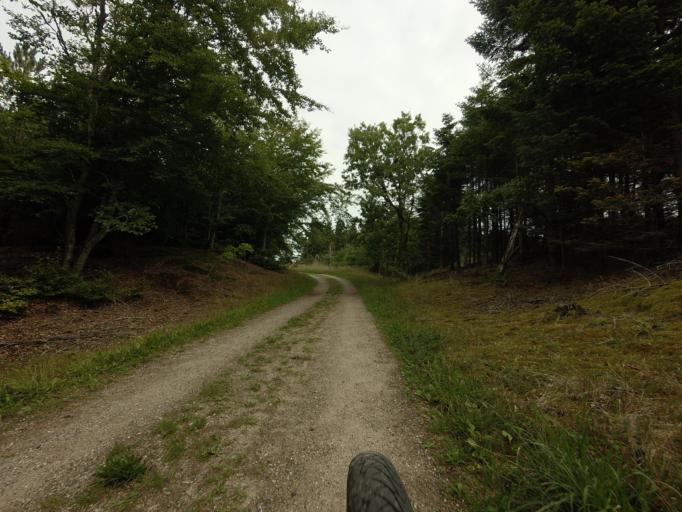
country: DK
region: North Denmark
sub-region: Hjorring Kommune
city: Hirtshals
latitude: 57.5513
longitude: 9.9203
